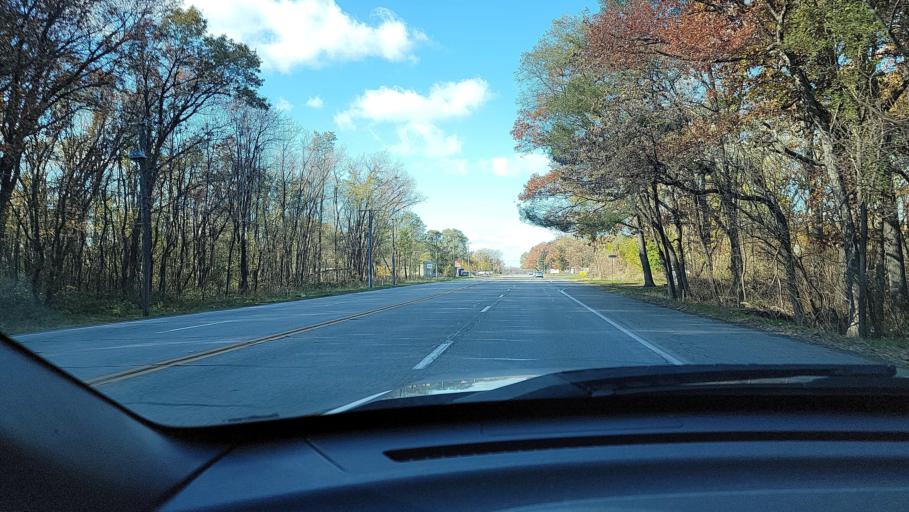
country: US
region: Indiana
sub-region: Porter County
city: Portage
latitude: 41.5988
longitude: -87.1620
